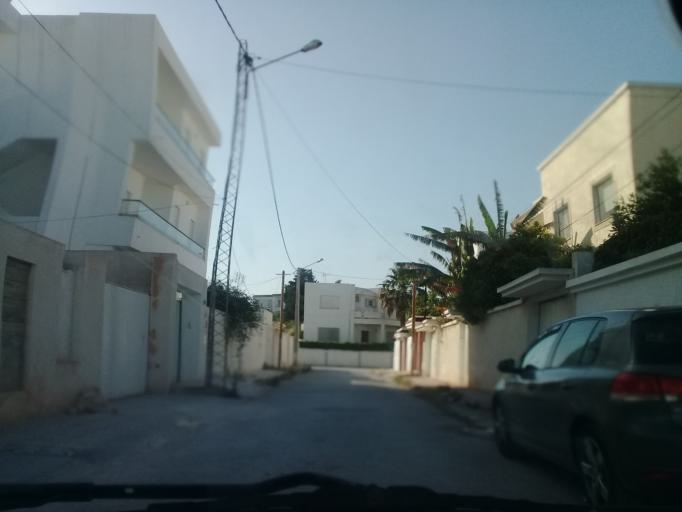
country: TN
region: Ariana
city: Ariana
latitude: 36.8362
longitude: 10.1963
